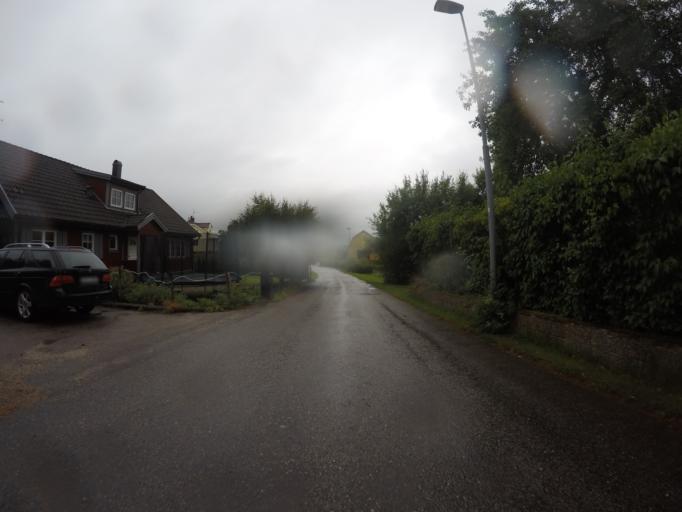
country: SE
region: Vaestra Goetaland
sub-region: Trollhattan
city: Sjuntorp
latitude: 58.1851
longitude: 12.2285
